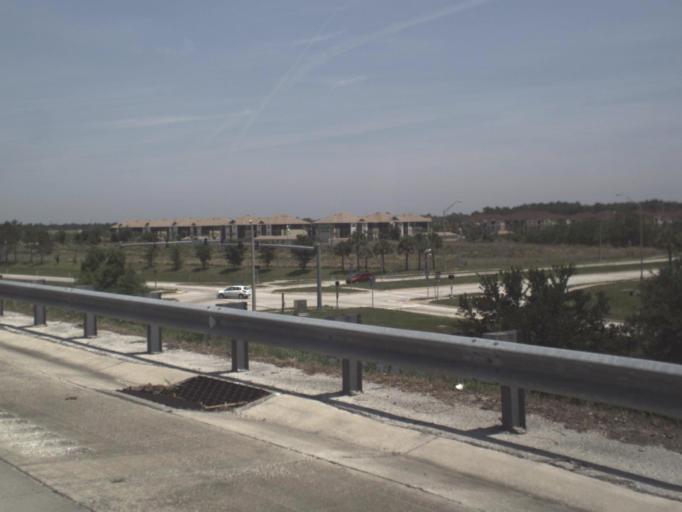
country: US
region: Florida
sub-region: Saint Johns County
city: Ponte Vedra Beach
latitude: 30.2150
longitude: -81.5138
